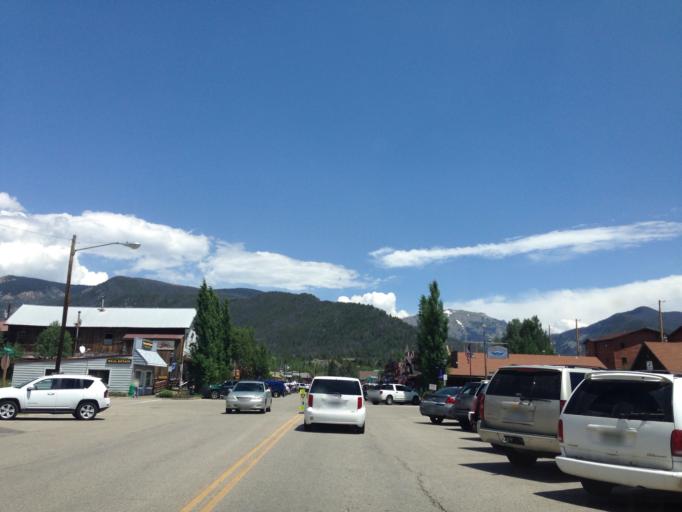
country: US
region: Colorado
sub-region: Grand County
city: Granby
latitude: 40.2521
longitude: -105.8219
